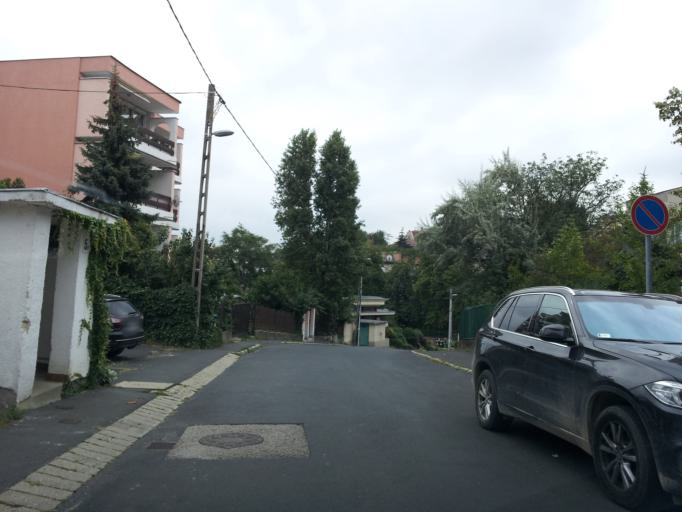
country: HU
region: Budapest
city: Budapest II. keruelet
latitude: 47.5196
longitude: 19.0130
